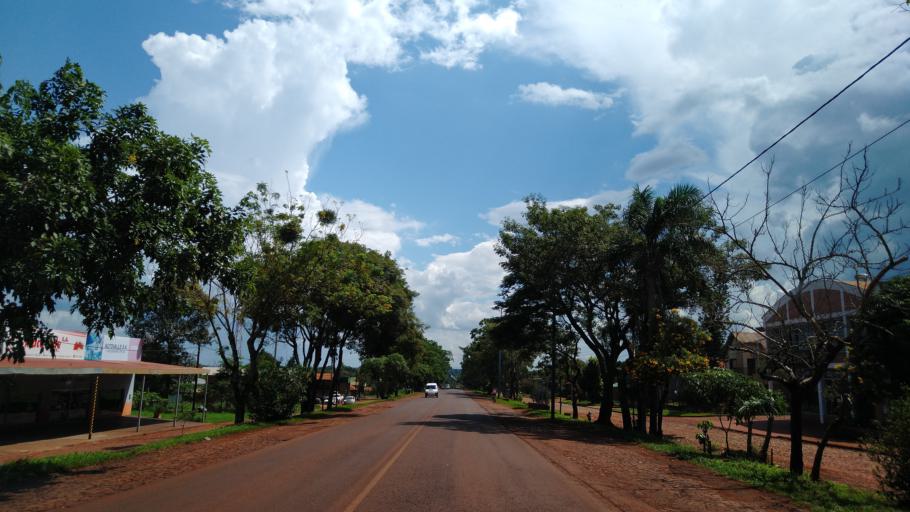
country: AR
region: Misiones
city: Puerto Libertad
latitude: -25.9703
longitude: -54.5739
